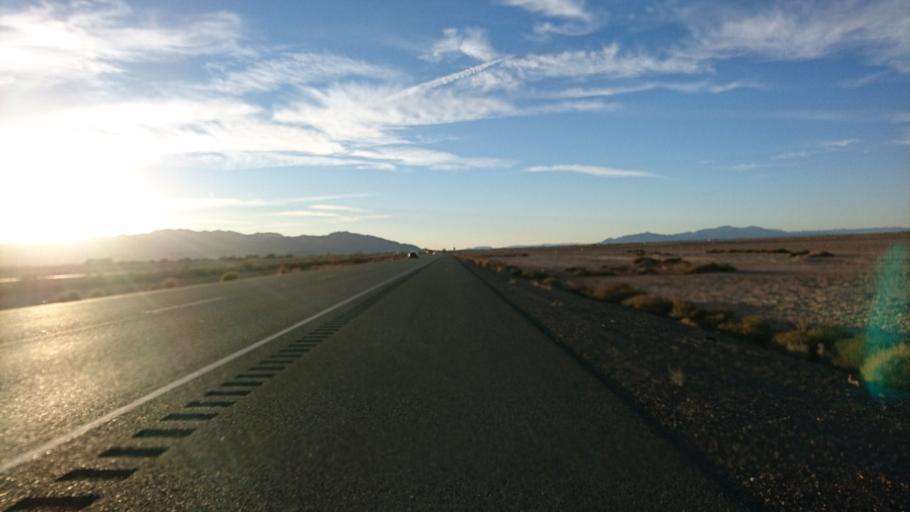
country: US
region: California
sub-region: San Bernardino County
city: Fort Irwin
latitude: 34.8040
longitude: -116.5403
